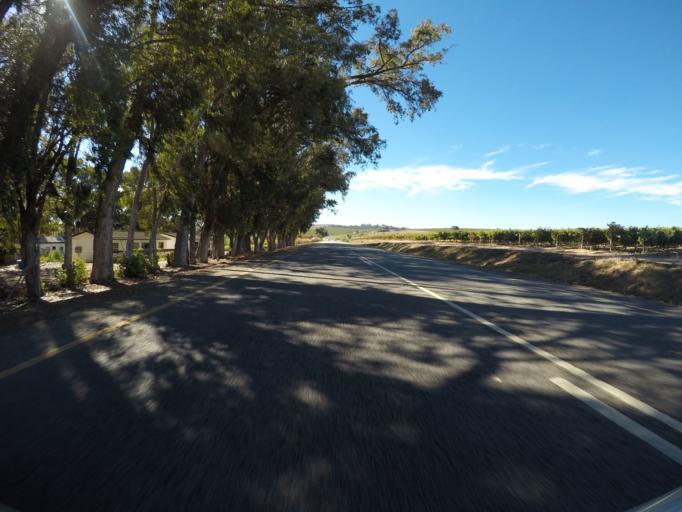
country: ZA
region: Western Cape
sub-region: Cape Winelands District Municipality
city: Stellenbosch
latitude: -33.9818
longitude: 18.7544
